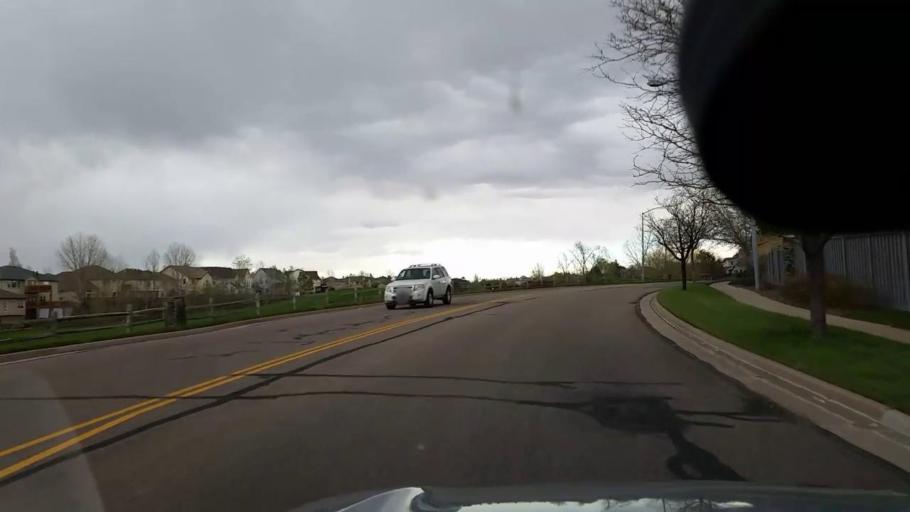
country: US
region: Colorado
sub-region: Adams County
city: Northglenn
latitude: 39.9405
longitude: -104.9768
